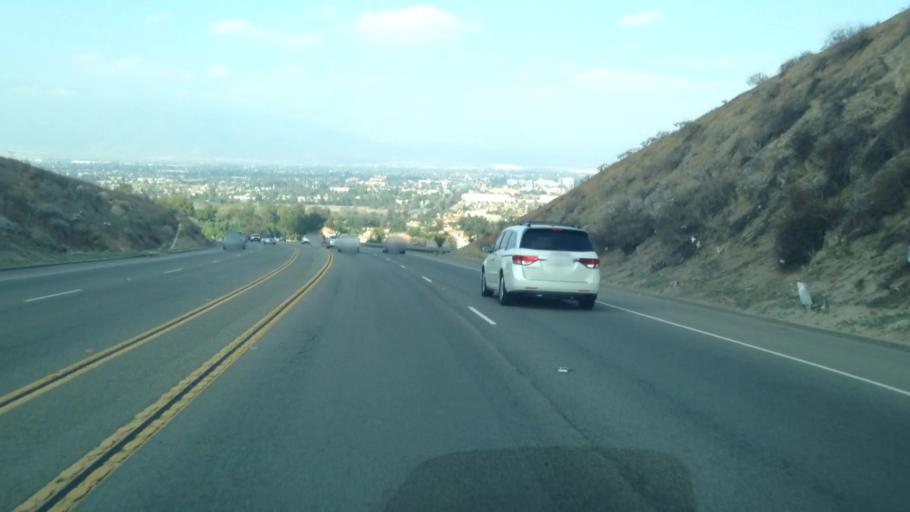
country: US
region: California
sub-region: Riverside County
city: Sunnyslope
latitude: 34.0397
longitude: -117.4337
